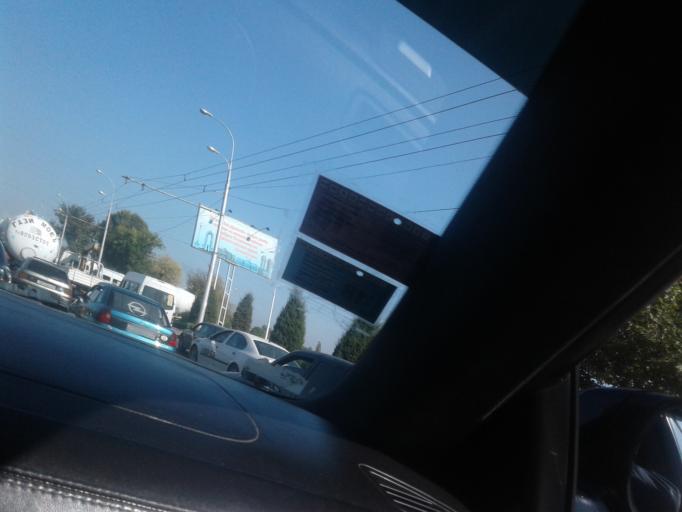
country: TJ
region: Dushanbe
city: Dushanbe
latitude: 38.5597
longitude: 68.7684
